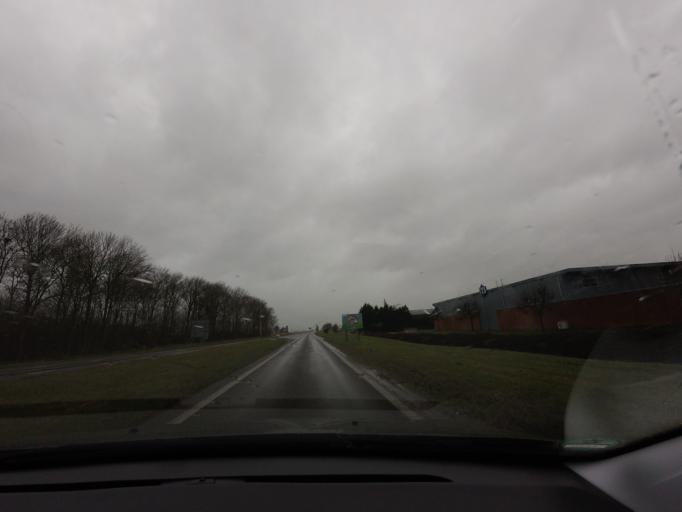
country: NL
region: Friesland
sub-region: Sudwest Fryslan
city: Bolsward
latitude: 53.0637
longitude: 5.5092
